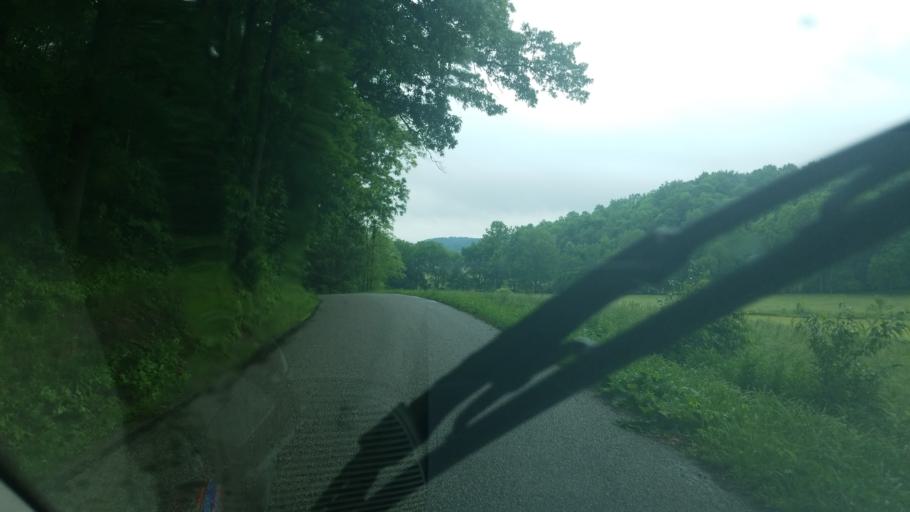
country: US
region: Ohio
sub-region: Sandusky County
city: Bellville
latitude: 40.6115
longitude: -82.4592
